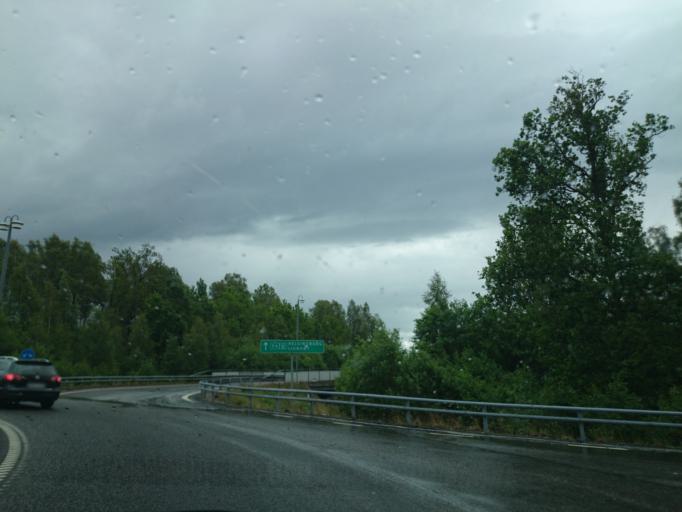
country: SE
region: Joenkoeping
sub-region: Varnamo Kommun
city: Varnamo
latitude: 57.1656
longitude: 14.0696
